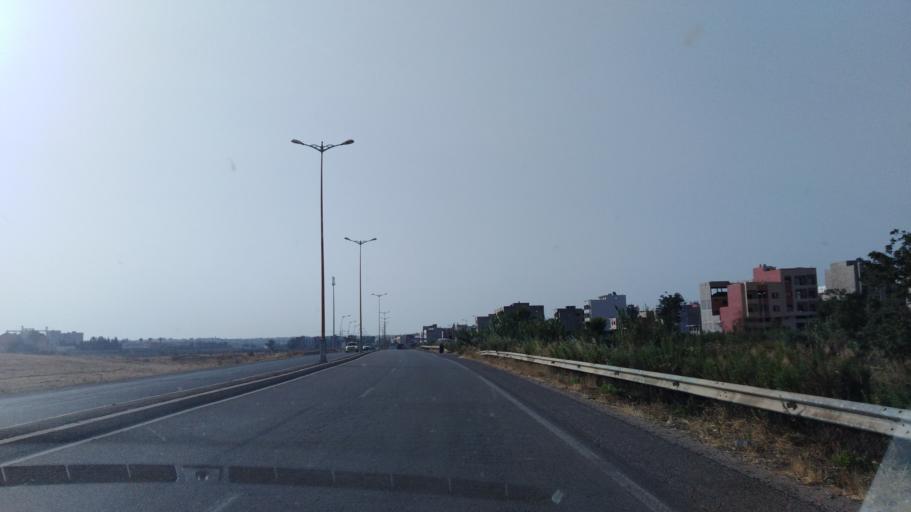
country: MA
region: Chaouia-Ouardigha
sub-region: Settat Province
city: Settat
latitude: 32.9789
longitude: -7.6055
